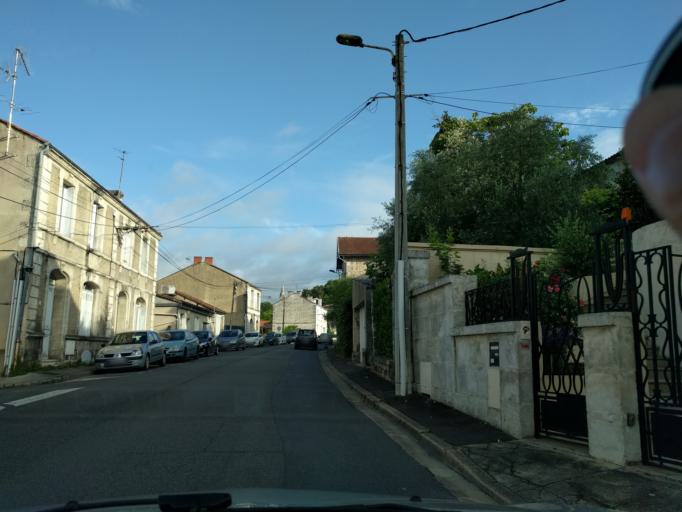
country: FR
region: Poitou-Charentes
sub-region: Departement de la Charente
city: Angouleme
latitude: 45.6465
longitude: 0.1511
